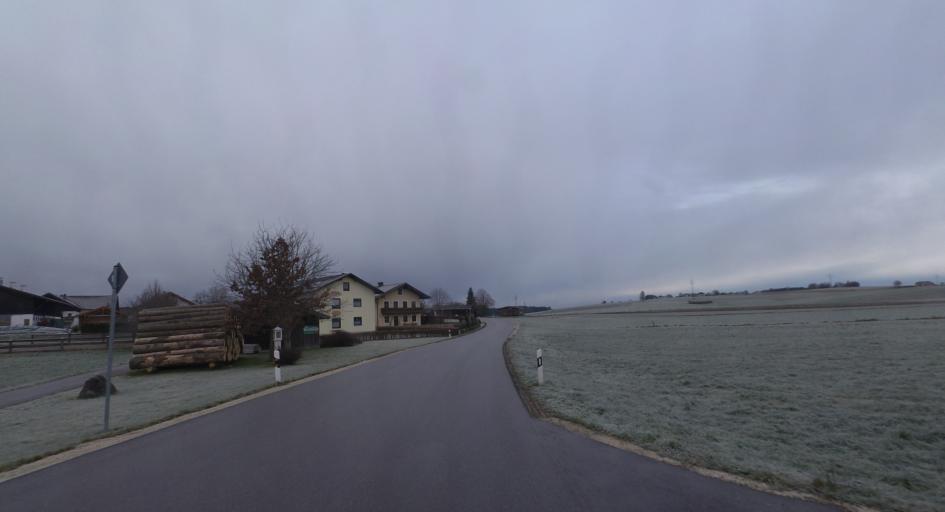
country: DE
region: Bavaria
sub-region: Upper Bavaria
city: Traunreut
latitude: 47.9432
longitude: 12.6341
